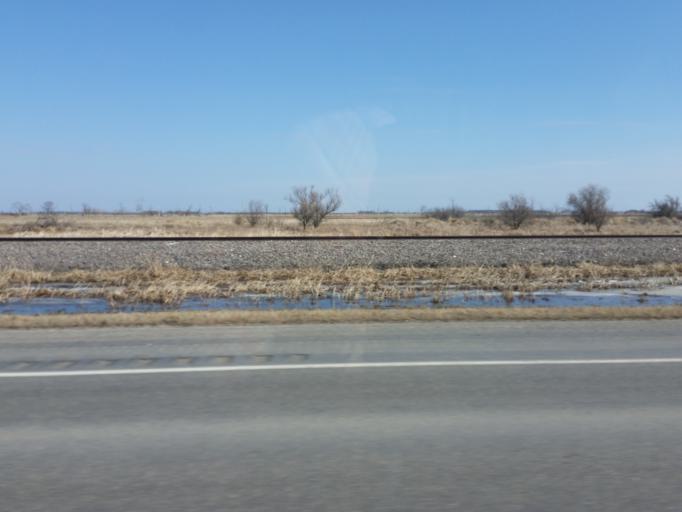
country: US
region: North Dakota
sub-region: Walsh County
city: Grafton
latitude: 48.2560
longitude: -97.3640
